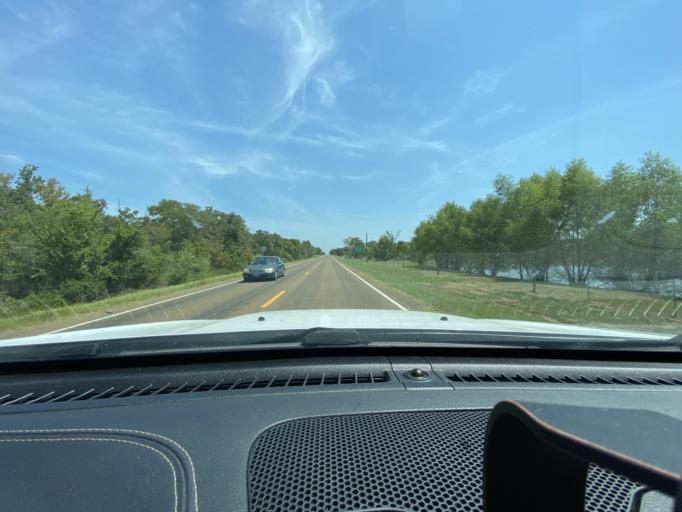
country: US
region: Texas
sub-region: Bastrop County
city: Smithville
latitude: 30.0605
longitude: -97.1034
